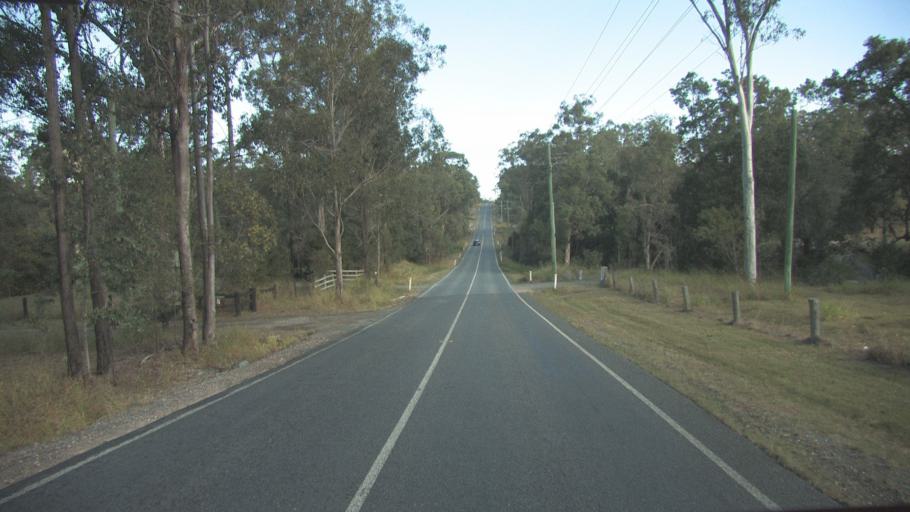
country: AU
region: Queensland
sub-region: Logan
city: Cedar Vale
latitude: -27.8264
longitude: 153.0538
